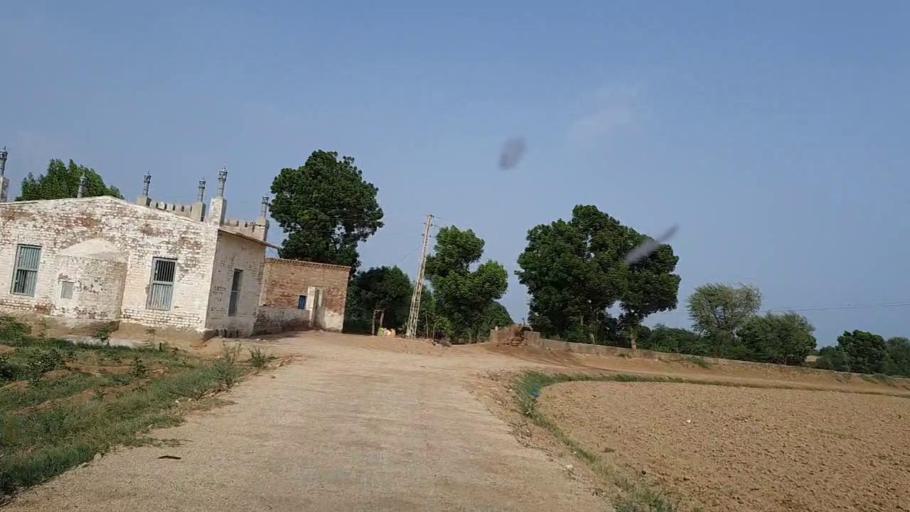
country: PK
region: Sindh
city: Kotri
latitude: 25.2469
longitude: 68.2509
